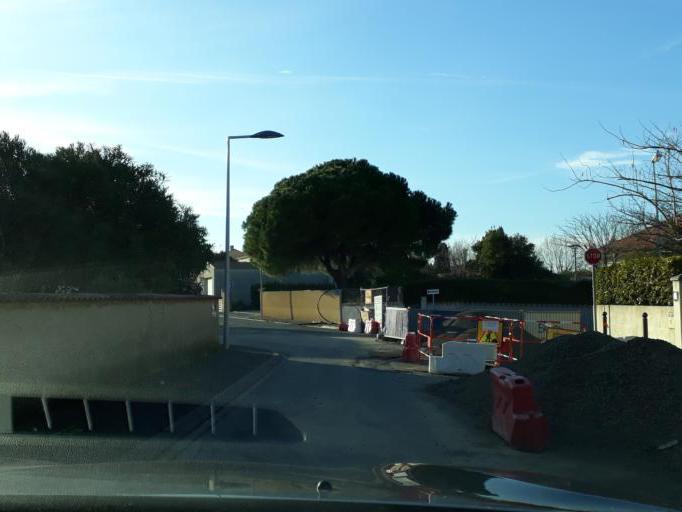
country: FR
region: Languedoc-Roussillon
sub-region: Departement de l'Herault
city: Marseillan
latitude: 43.3547
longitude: 3.5249
